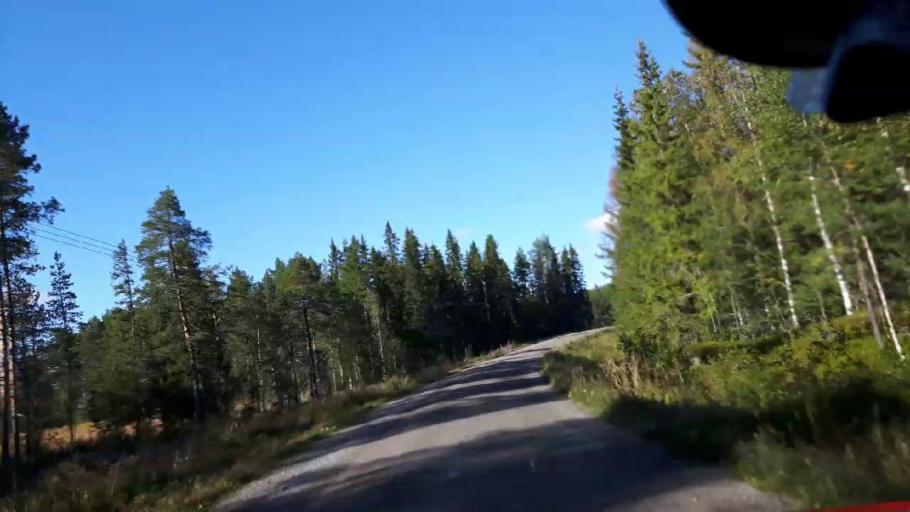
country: SE
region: Jaemtland
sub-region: Ragunda Kommun
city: Hammarstrand
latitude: 63.5233
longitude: 16.0559
